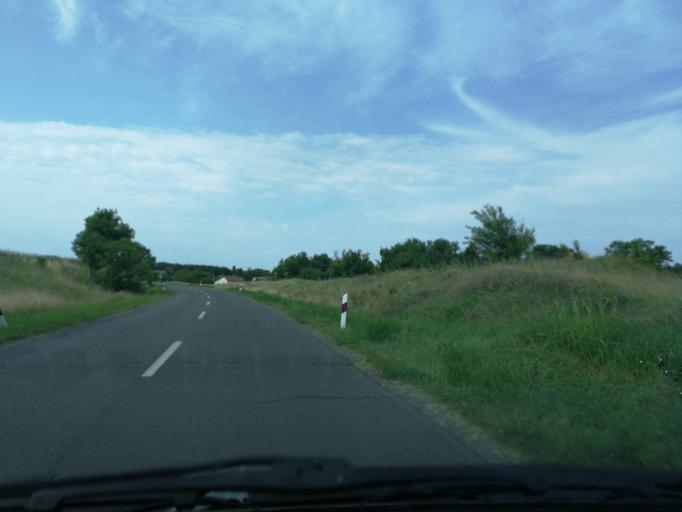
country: HU
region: Bacs-Kiskun
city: Davod
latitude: 46.0011
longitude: 18.9246
